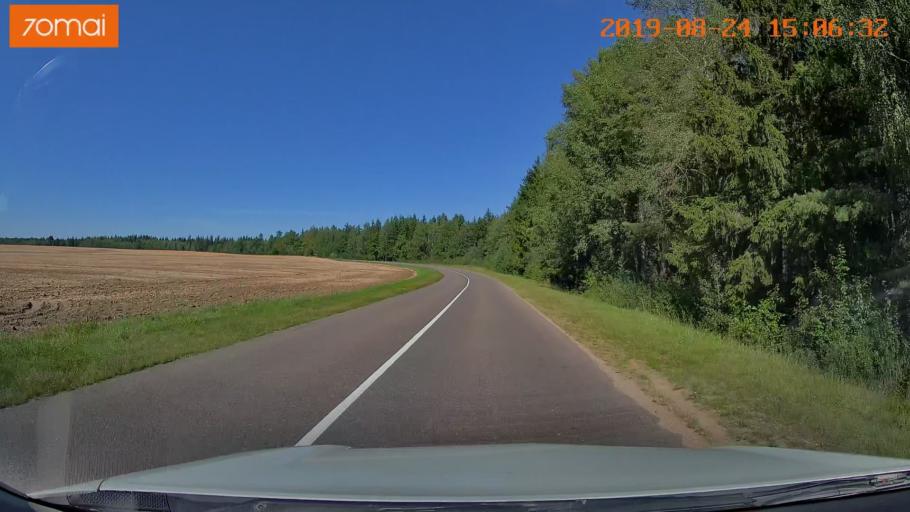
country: BY
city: Michanovichi
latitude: 53.6013
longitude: 27.6785
